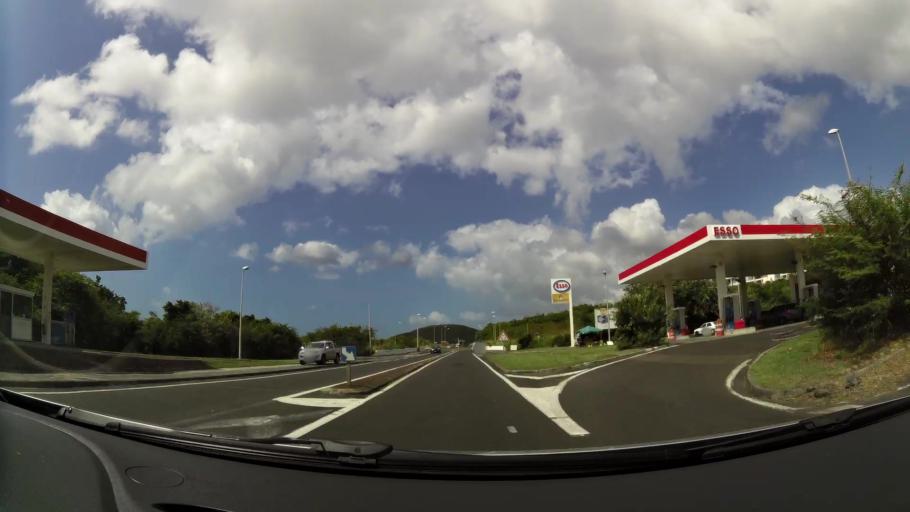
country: MQ
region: Martinique
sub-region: Martinique
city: Fort-de-France
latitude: 14.6358
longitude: -61.1352
